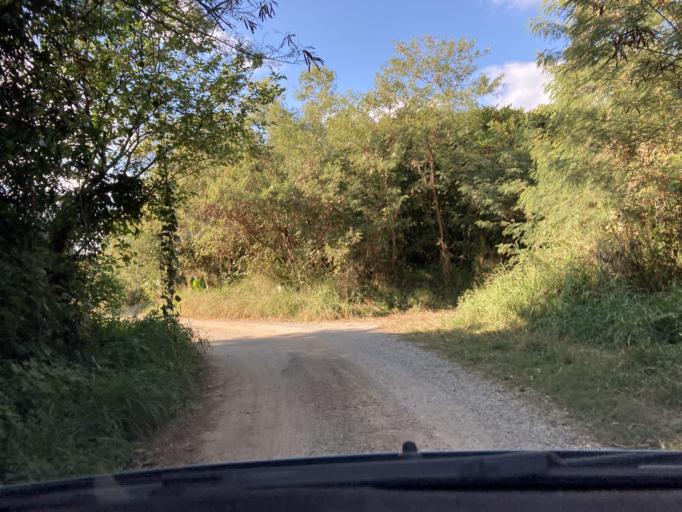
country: JP
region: Okinawa
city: Katsuren-haebaru
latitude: 26.3200
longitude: 127.9239
